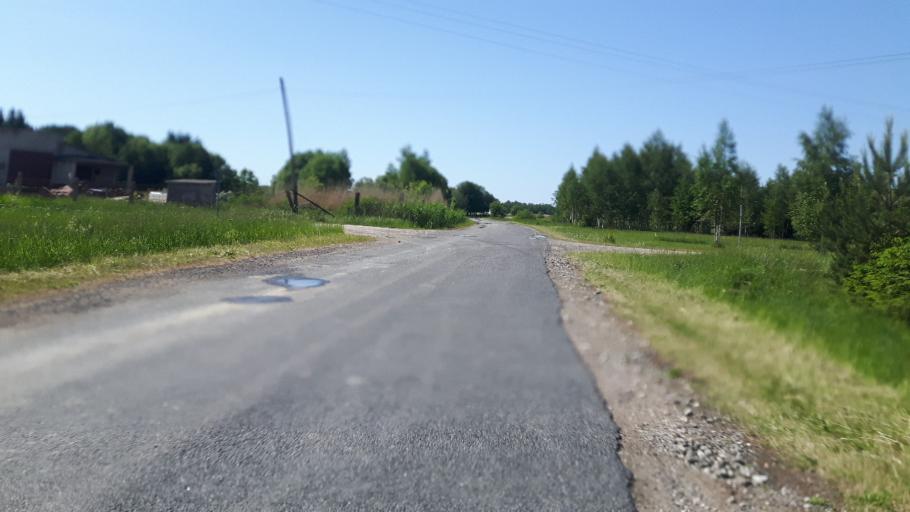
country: EE
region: Paernumaa
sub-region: Vaendra vald (alev)
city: Vandra
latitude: 58.5899
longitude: 25.0169
